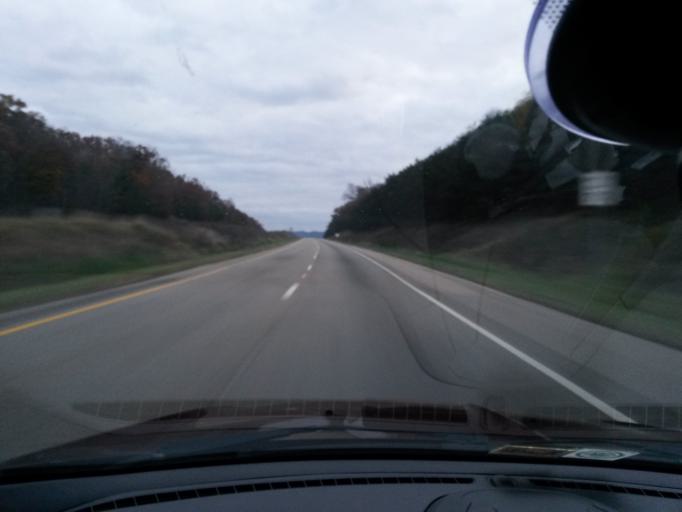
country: US
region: Virginia
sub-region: Alleghany County
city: Clifton Forge
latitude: 37.8271
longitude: -79.7824
